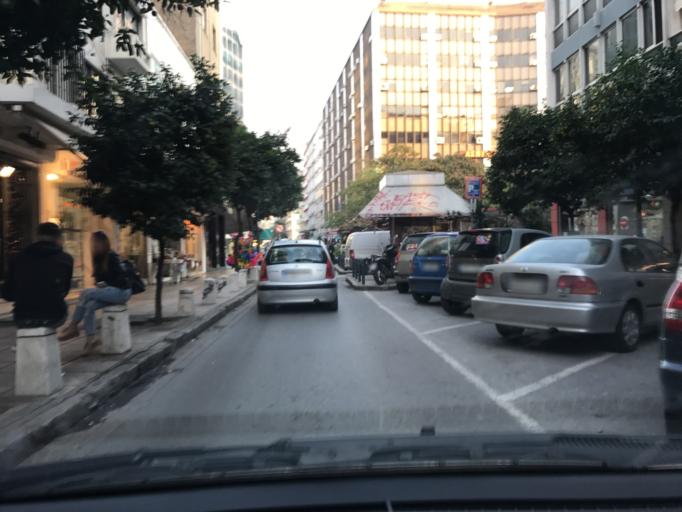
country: GR
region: Central Macedonia
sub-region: Nomos Thessalonikis
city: Thessaloniki
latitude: 40.6352
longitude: 22.9406
